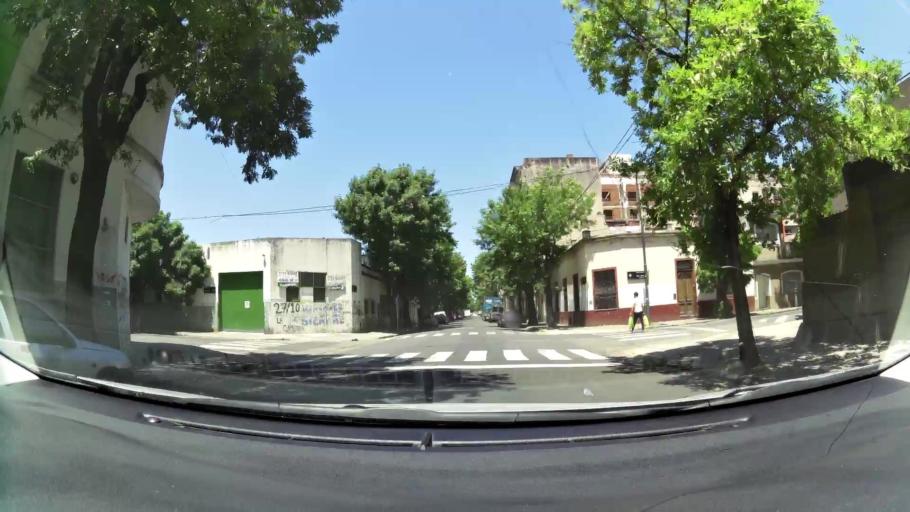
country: AR
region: Buenos Aires
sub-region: Partido de Avellaneda
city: Avellaneda
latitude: -34.6503
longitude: -58.3778
